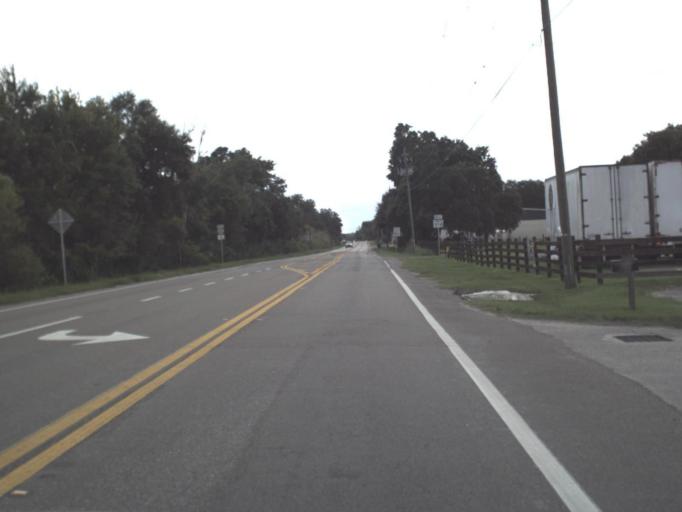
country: US
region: Florida
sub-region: Hillsborough County
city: Dover
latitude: 27.9896
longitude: -82.2447
